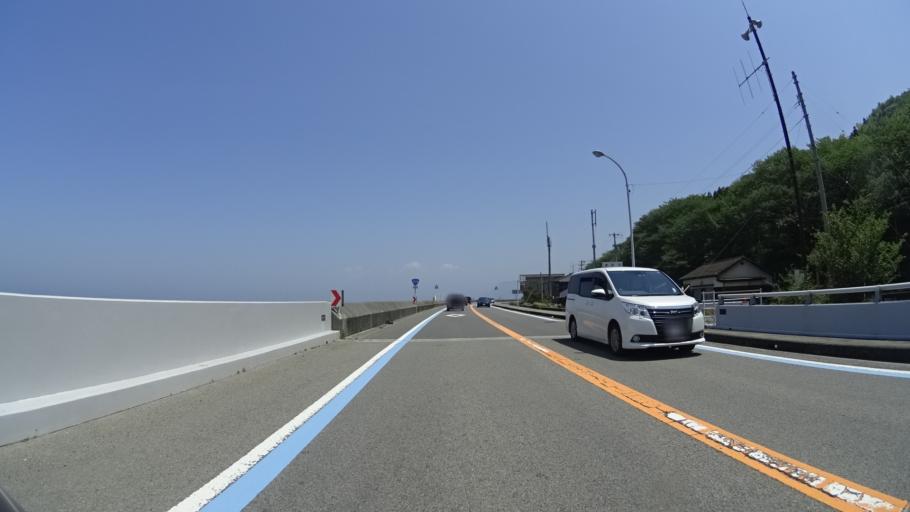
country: JP
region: Ehime
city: Ozu
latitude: 33.6375
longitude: 132.5311
